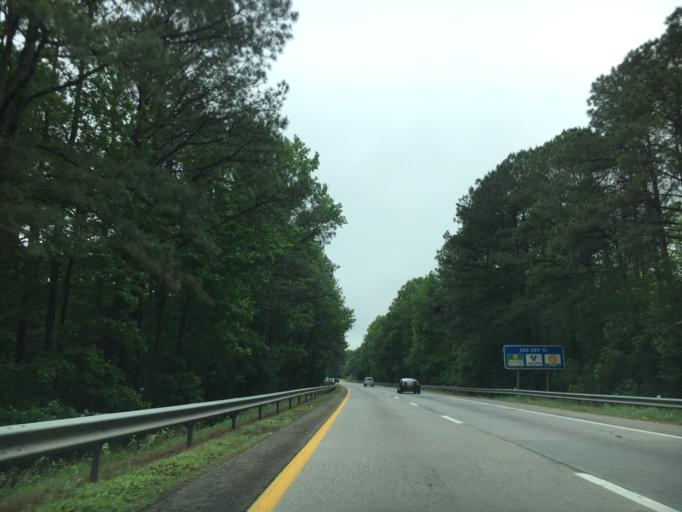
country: US
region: Virginia
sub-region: Chesterfield County
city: Matoaca
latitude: 37.1941
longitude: -77.4841
